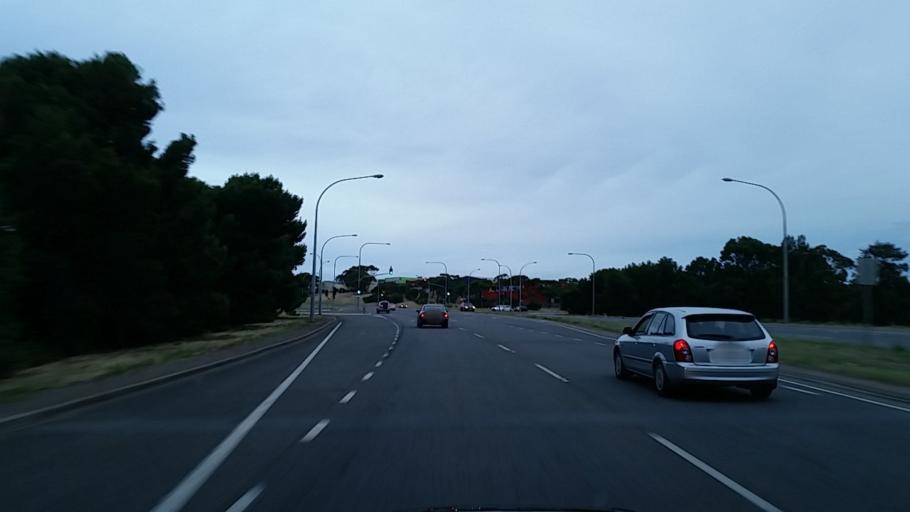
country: AU
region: South Australia
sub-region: Onkaparinga
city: Morphett Vale
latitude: -35.1077
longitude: 138.4980
